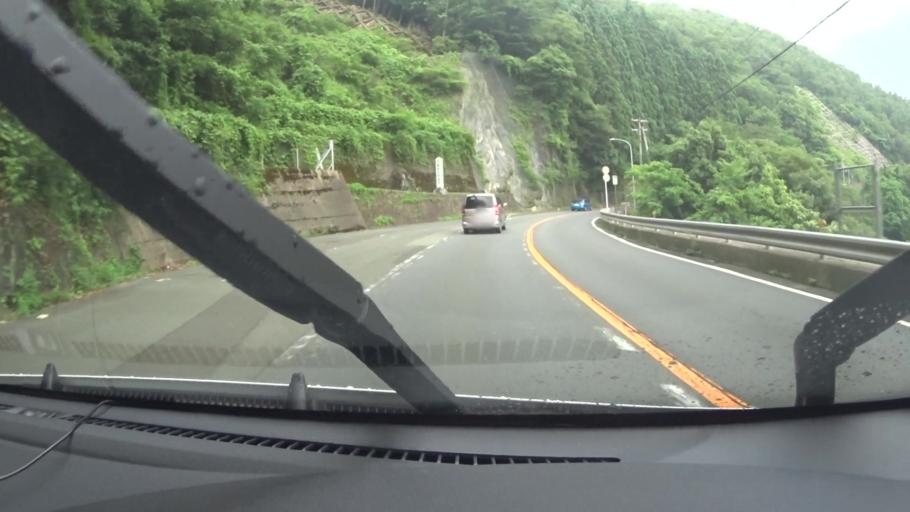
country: JP
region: Kyoto
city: Ayabe
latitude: 35.2412
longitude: 135.4169
